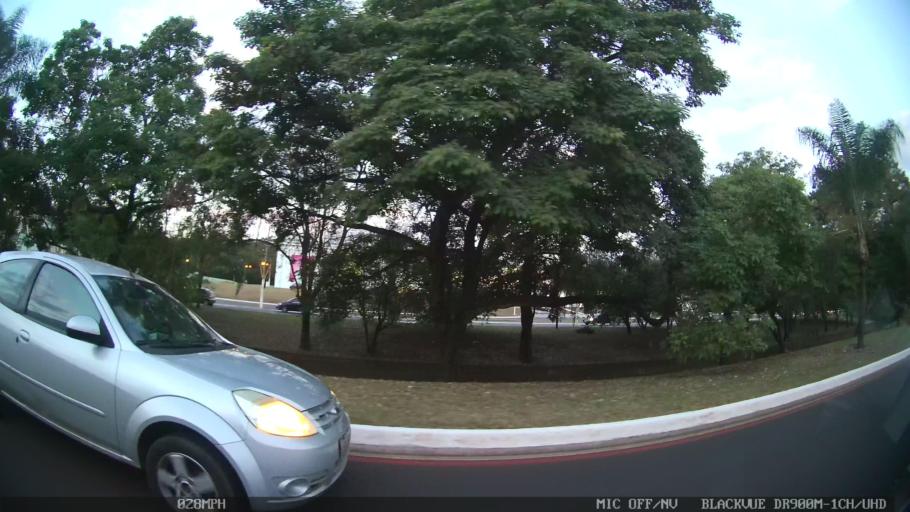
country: BR
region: Sao Paulo
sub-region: Ribeirao Preto
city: Ribeirao Preto
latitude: -21.1952
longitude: -47.7984
